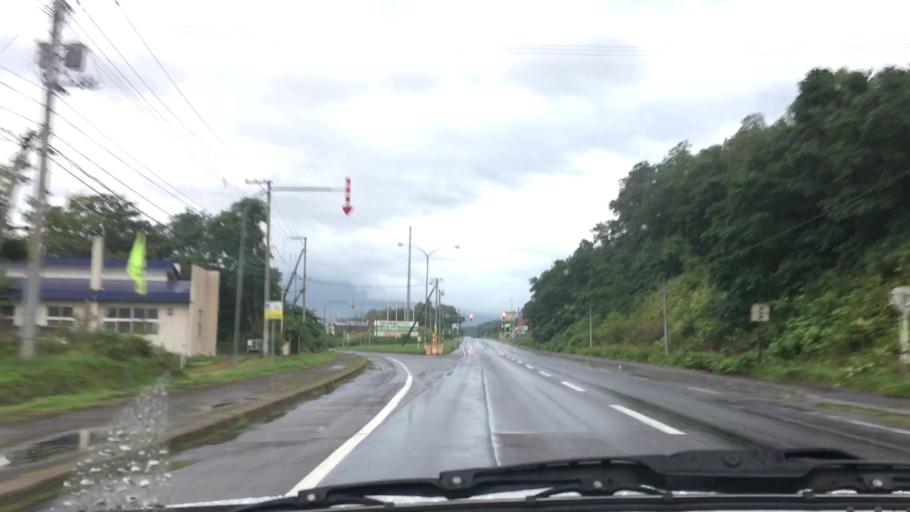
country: JP
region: Hokkaido
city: Nanae
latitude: 42.1128
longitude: 140.5462
